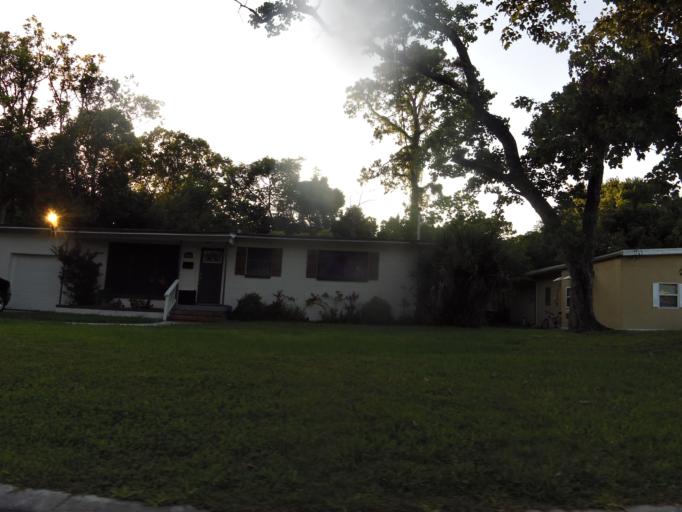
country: US
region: Florida
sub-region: Duval County
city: Jacksonville
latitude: 30.2353
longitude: -81.6137
